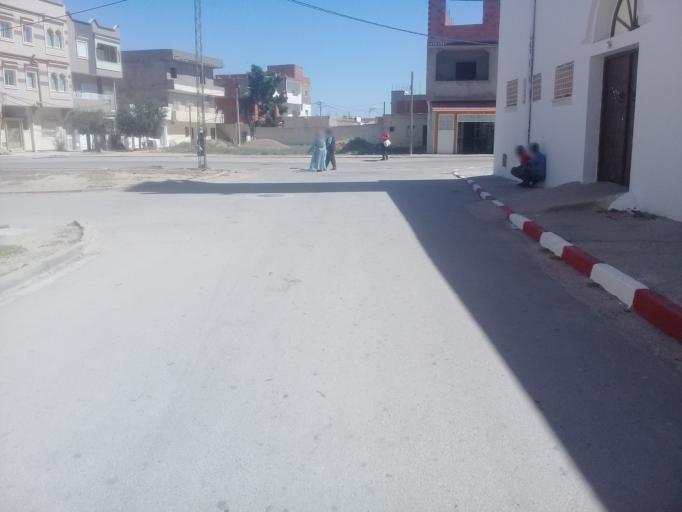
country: TN
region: Al Qayrawan
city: Kairouan
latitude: 35.6614
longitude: 10.1075
